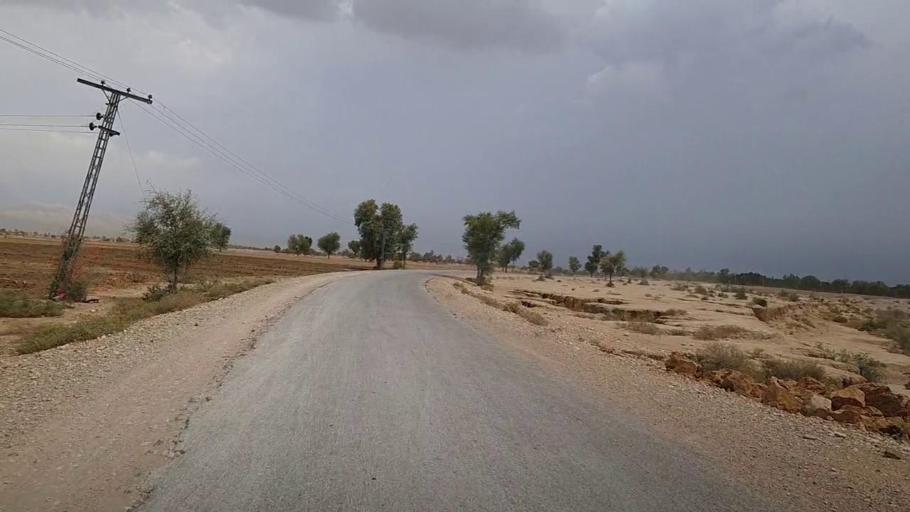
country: PK
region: Sindh
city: Sehwan
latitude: 26.3102
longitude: 67.7307
